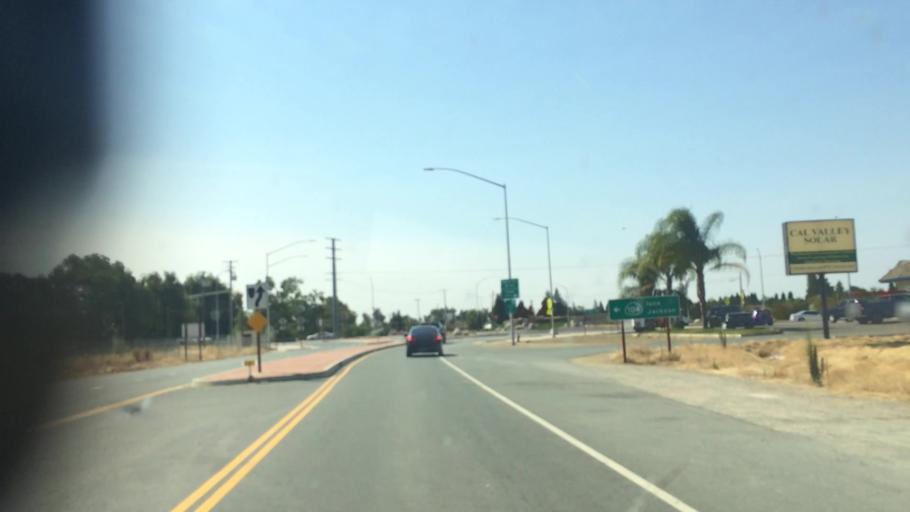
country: US
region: California
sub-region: Sacramento County
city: Galt
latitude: 38.2921
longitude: -121.3139
